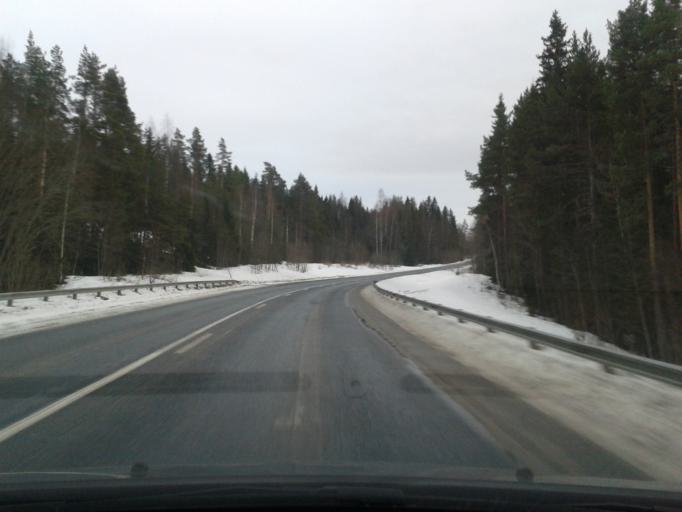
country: SE
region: Vaesternorrland
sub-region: Solleftea Kommun
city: As
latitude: 63.4132
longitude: 16.9659
